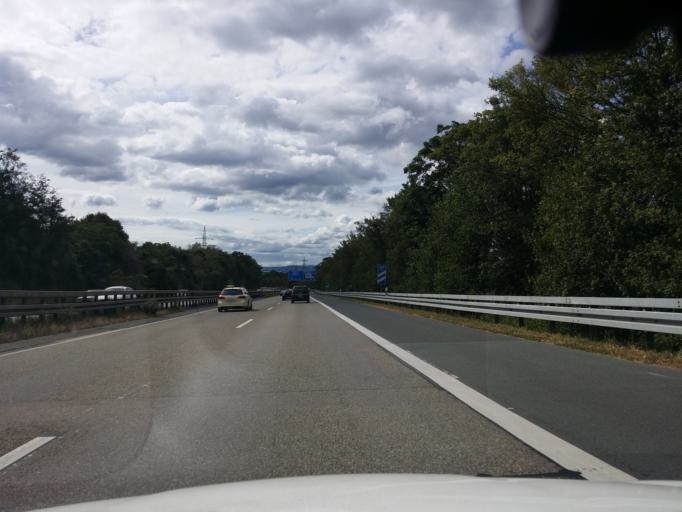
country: DE
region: Hesse
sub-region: Regierungsbezirk Darmstadt
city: Wiesbaden
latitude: 50.0524
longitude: 8.2703
